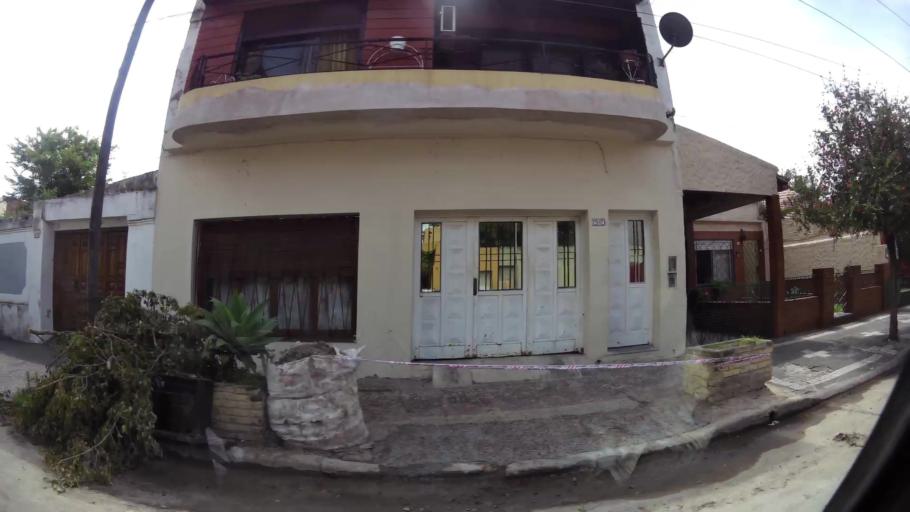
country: AR
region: Buenos Aires
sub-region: Partido de Avellaneda
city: Avellaneda
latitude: -34.6642
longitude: -58.4029
